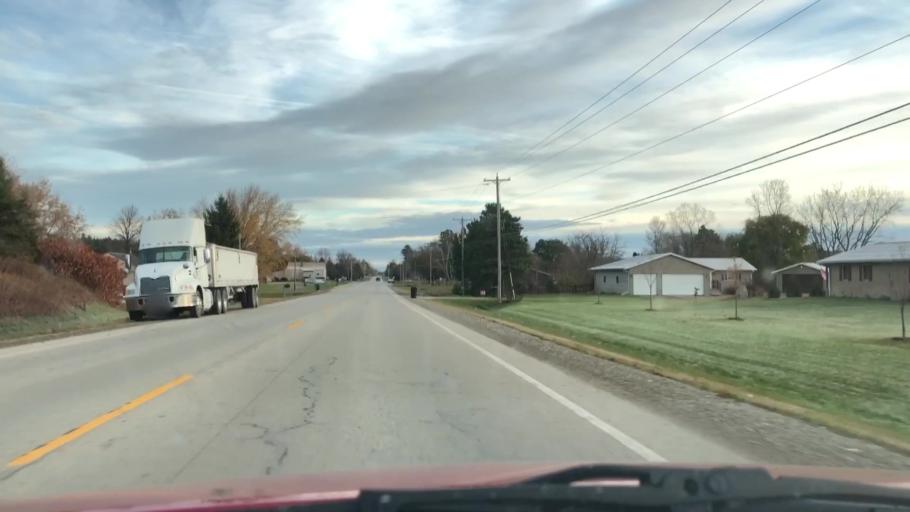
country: US
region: Wisconsin
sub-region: Brown County
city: Oneida
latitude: 44.4373
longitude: -88.2328
